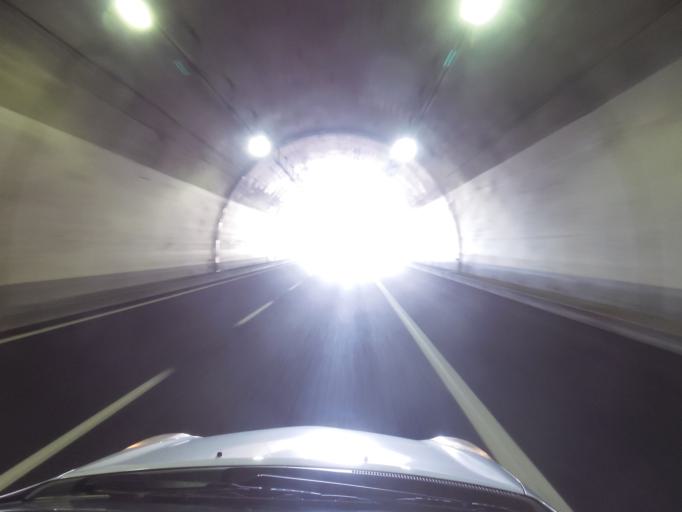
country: IT
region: Emilia-Romagna
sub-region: Provincia di Bologna
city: Marzabotto
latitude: 44.2897
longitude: 11.2071
